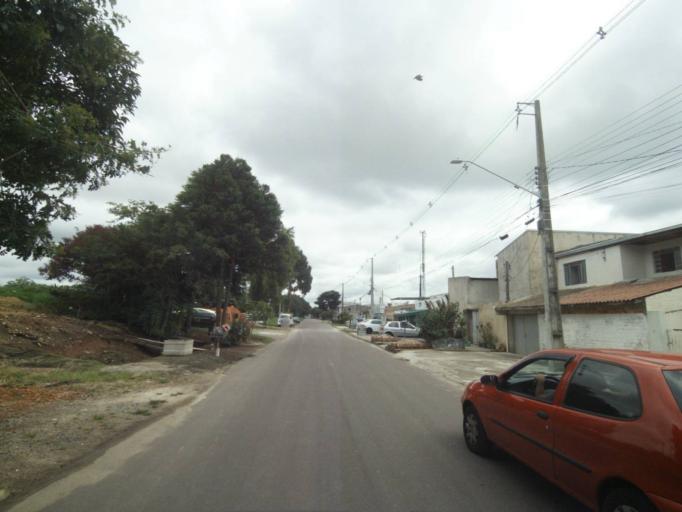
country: BR
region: Parana
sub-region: Pinhais
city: Pinhais
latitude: -25.4527
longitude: -49.2005
